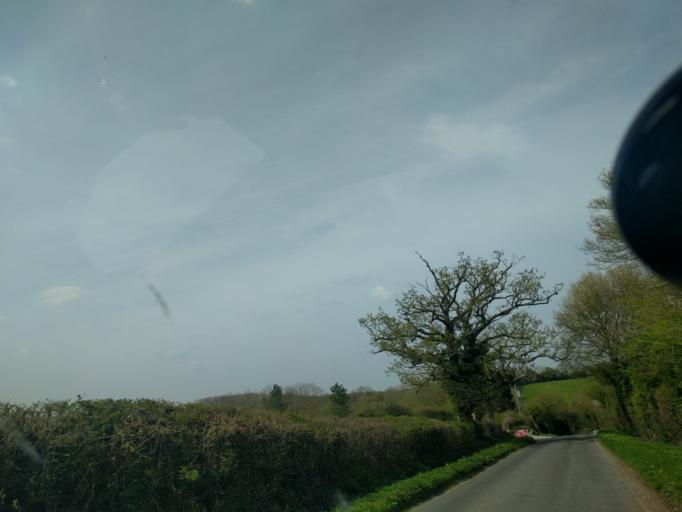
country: GB
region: England
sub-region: Wiltshire
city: Corsham
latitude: 51.4213
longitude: -2.1637
